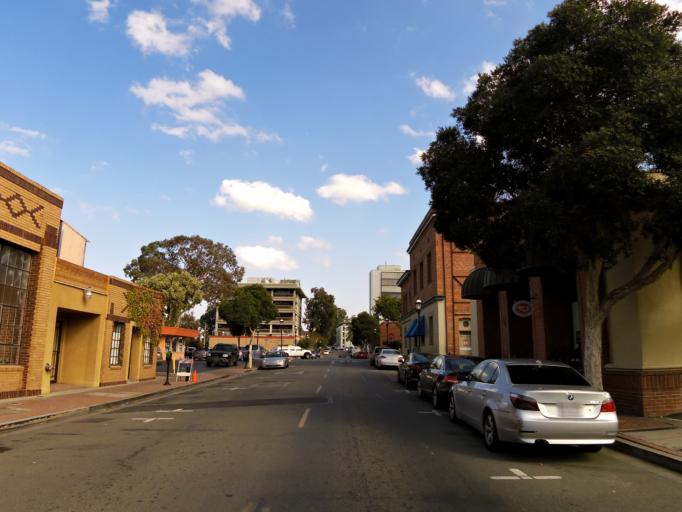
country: US
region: California
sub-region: Contra Costa County
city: Martinez
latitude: 38.0180
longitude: -122.1369
